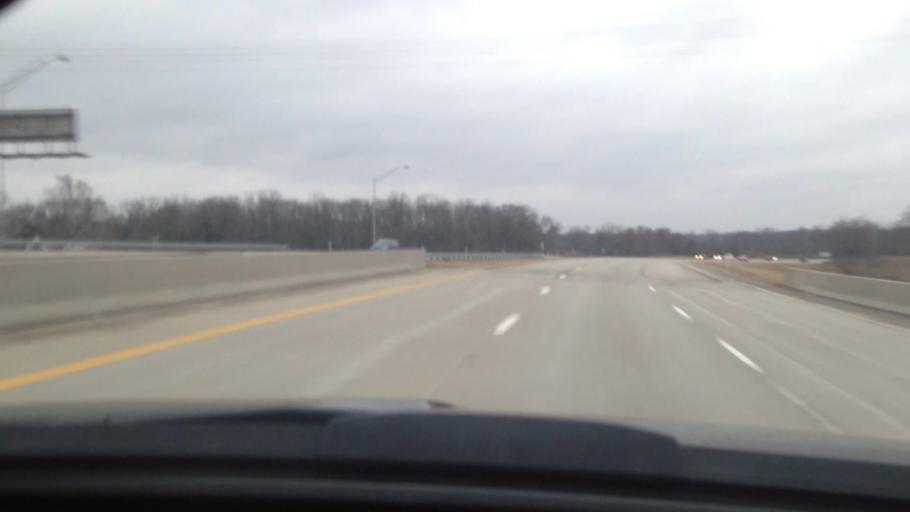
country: US
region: Indiana
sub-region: Delaware County
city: Muncie
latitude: 40.1786
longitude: -85.3366
